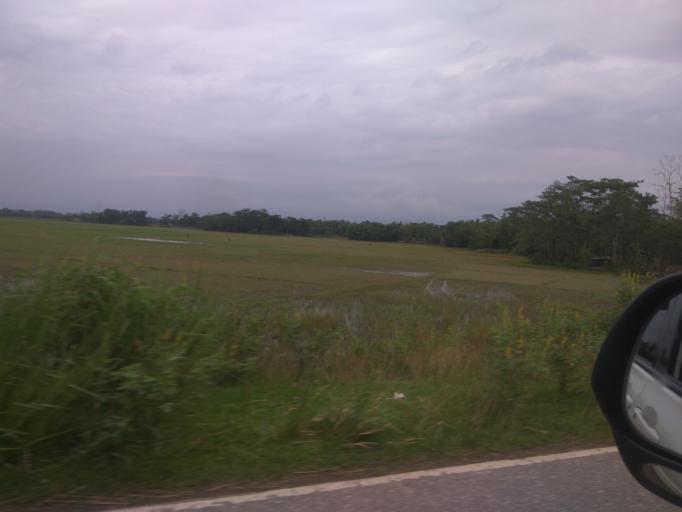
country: IN
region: Assam
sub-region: Karimganj
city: Karimganj
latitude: 24.9470
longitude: 92.2367
